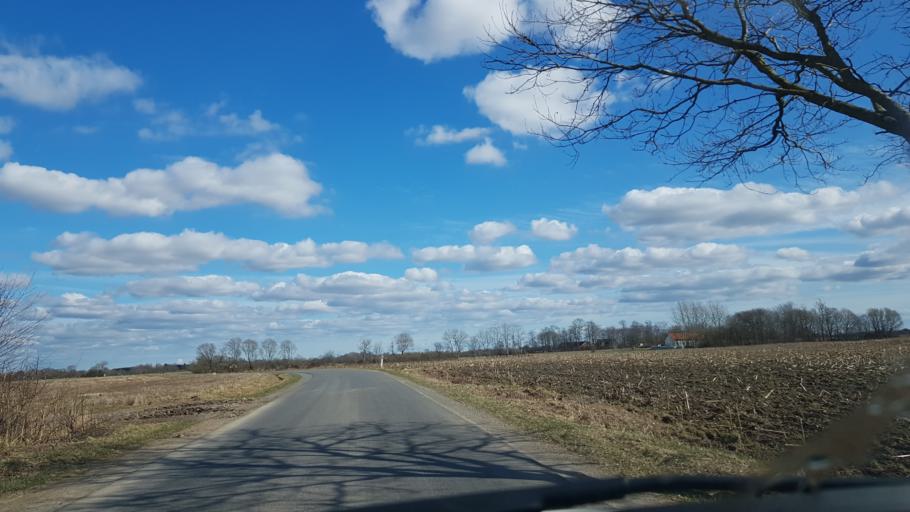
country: DK
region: South Denmark
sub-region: Kolding Kommune
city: Vamdrup
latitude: 55.4067
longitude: 9.2068
